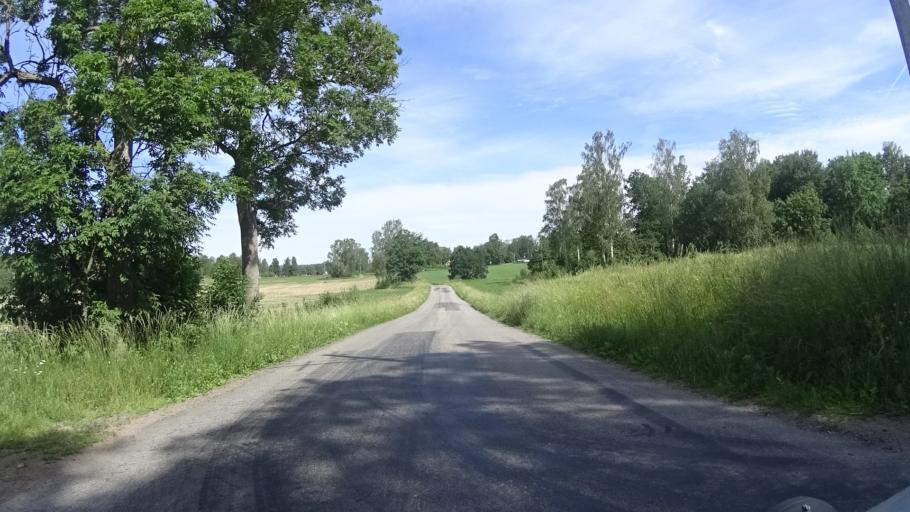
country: SE
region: Kalmar
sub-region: Vasterviks Kommun
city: Overum
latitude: 57.8866
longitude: 16.1728
